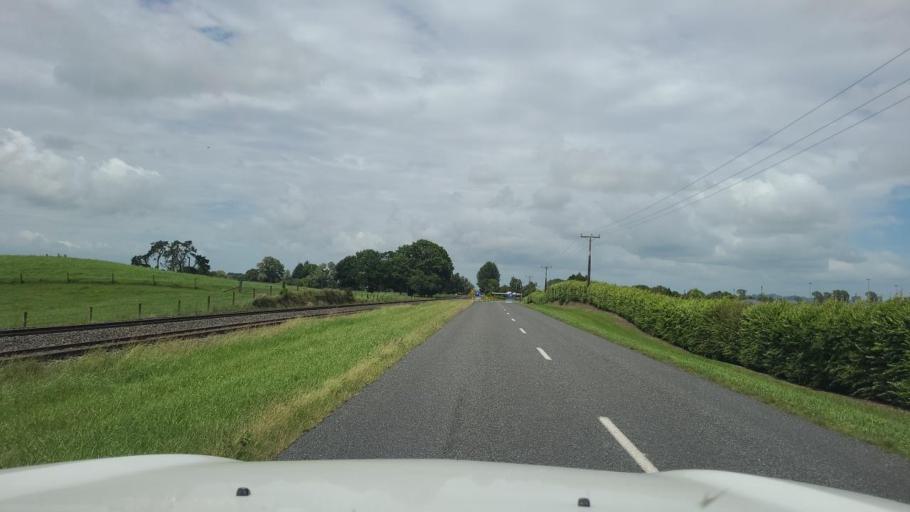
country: NZ
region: Waikato
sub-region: Matamata-Piako District
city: Matamata
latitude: -37.8755
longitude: 175.7579
